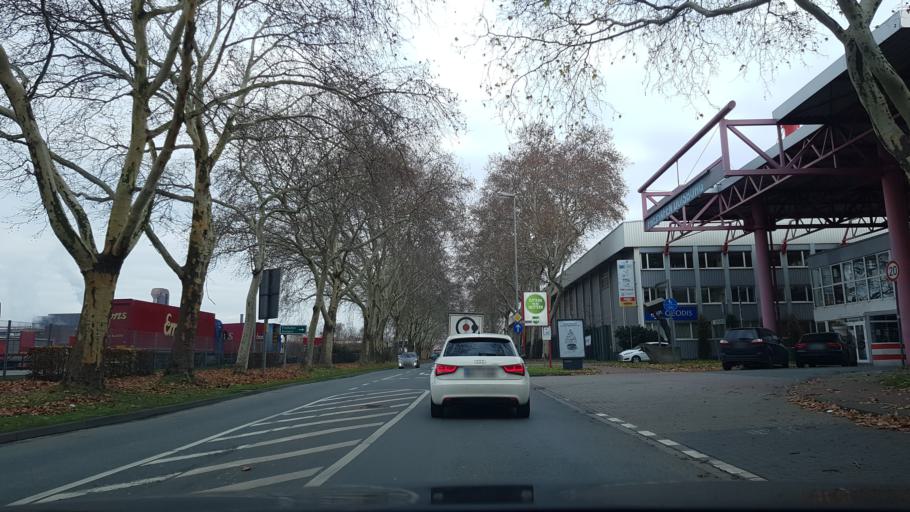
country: DE
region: North Rhine-Westphalia
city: Meiderich
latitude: 51.4576
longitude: 6.7477
